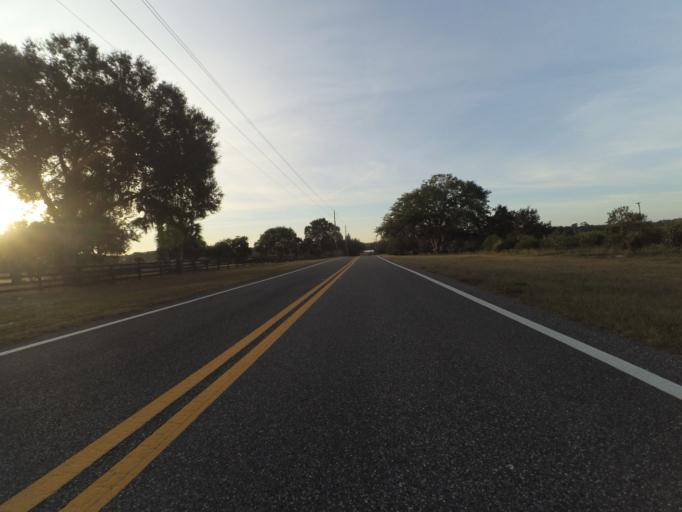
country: US
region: Florida
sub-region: Lake County
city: Umatilla
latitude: 28.9478
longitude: -81.6790
